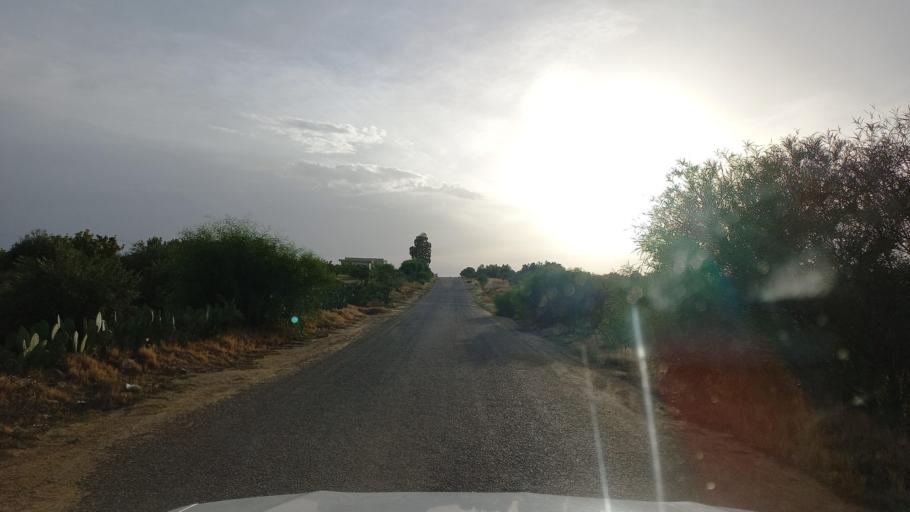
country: TN
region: Al Qasrayn
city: Kasserine
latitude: 35.2213
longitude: 9.0541
